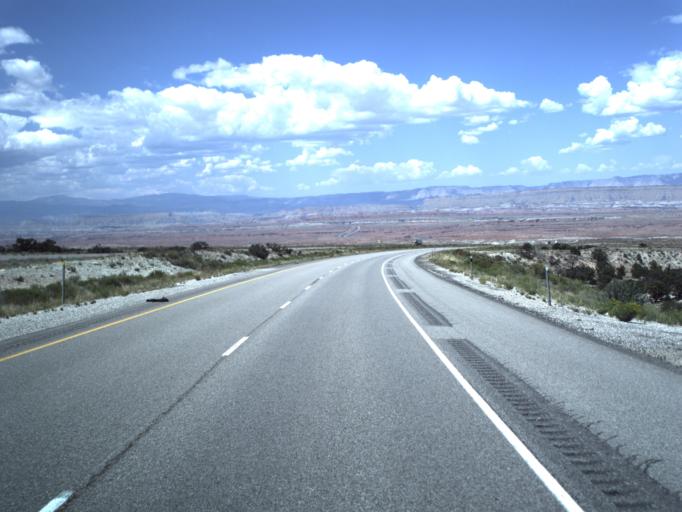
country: US
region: Utah
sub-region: Emery County
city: Ferron
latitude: 38.8416
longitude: -110.9590
